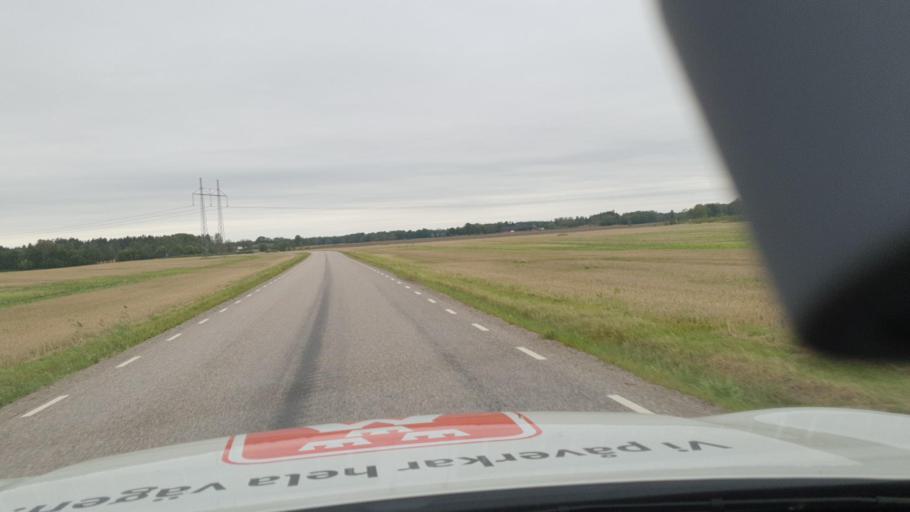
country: SE
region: Vaestra Goetaland
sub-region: Vanersborgs Kommun
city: Vanersborg
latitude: 58.4955
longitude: 12.2290
